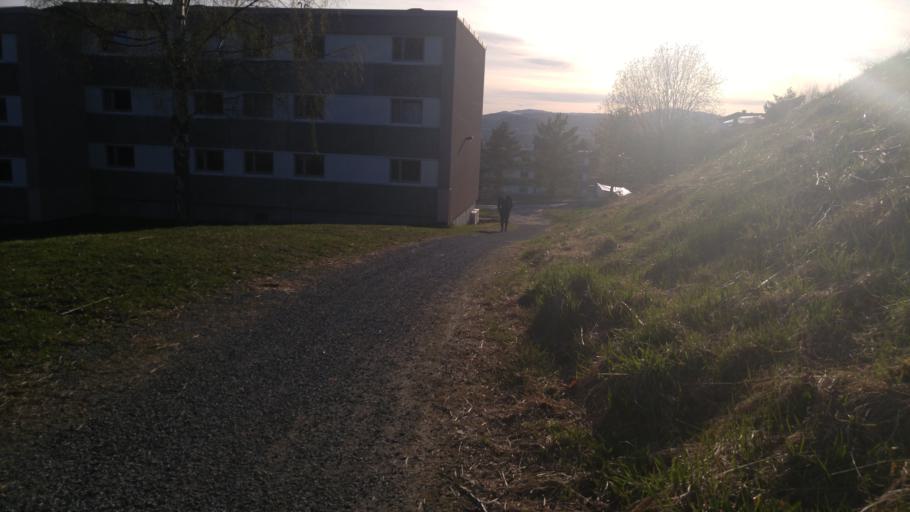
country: NO
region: Sor-Trondelag
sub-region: Trondheim
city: Trondheim
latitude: 63.4069
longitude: 10.4483
